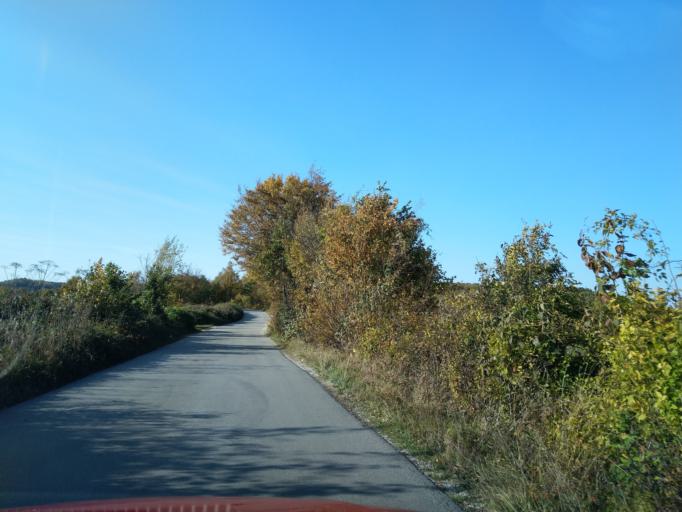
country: RS
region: Central Serbia
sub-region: Zlatiborski Okrug
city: Uzice
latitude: 43.8650
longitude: 19.7660
